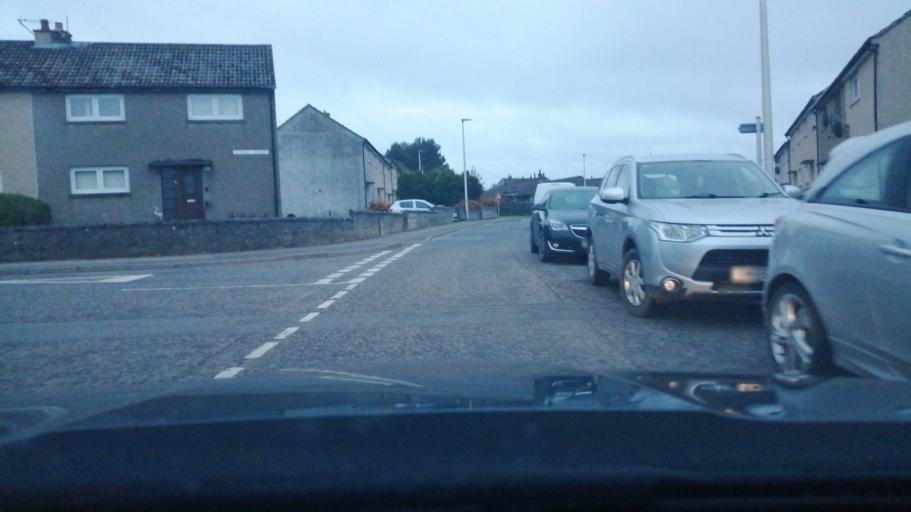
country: GB
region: Scotland
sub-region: Moray
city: Keith
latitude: 57.5387
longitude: -2.9566
